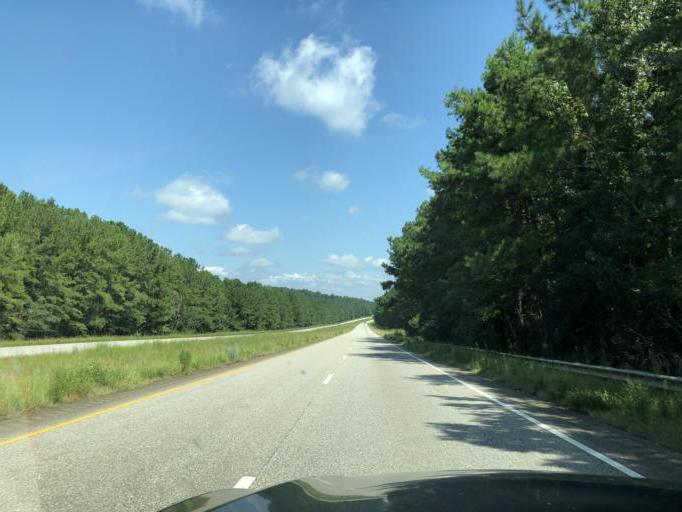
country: US
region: Alabama
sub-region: Henry County
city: Abbeville
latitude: 31.7304
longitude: -85.2556
